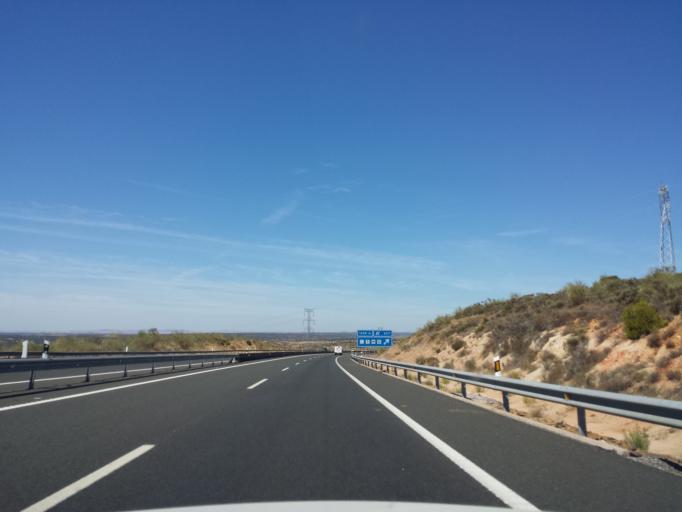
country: ES
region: Extremadura
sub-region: Provincia de Caceres
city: Jaraicejo
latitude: 39.6625
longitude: -5.7719
